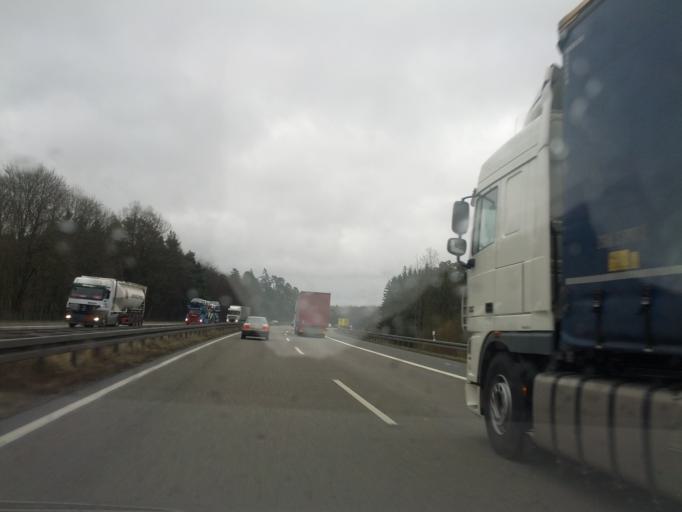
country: DE
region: Hesse
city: Romrod
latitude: 50.7125
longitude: 9.1750
